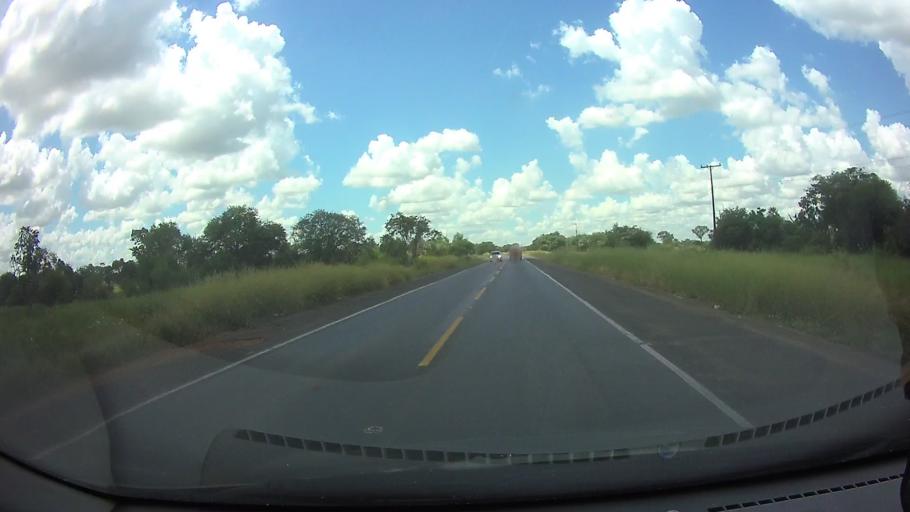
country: PY
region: Presidente Hayes
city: Nanawa
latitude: -25.1963
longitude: -57.6345
